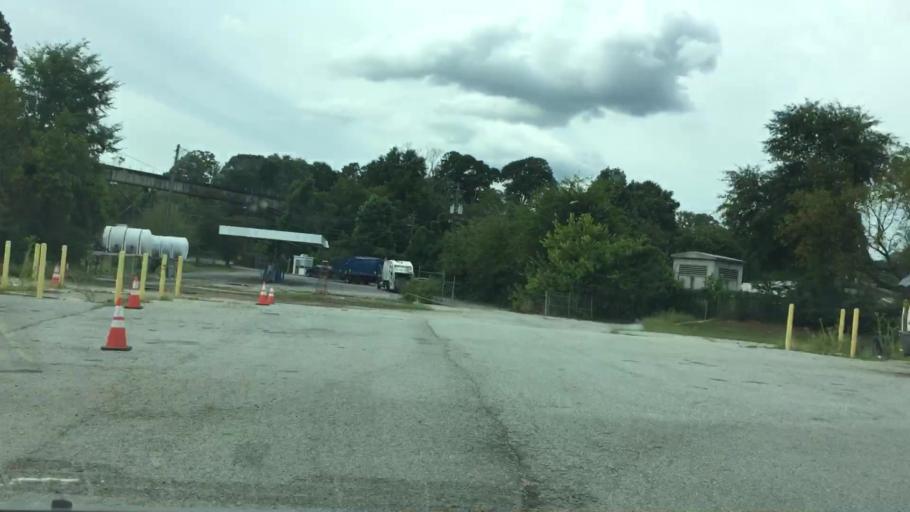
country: US
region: Georgia
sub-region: Fulton County
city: Atlanta
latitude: 33.7681
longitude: -84.4237
